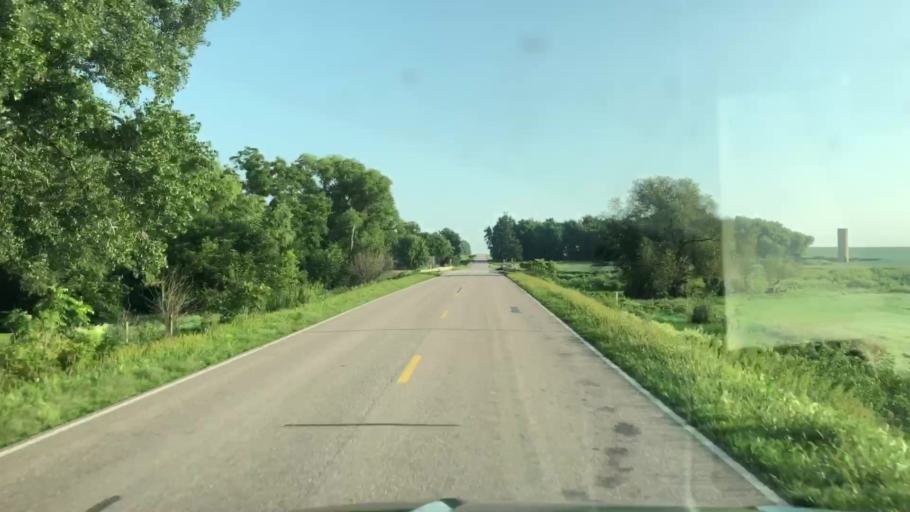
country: US
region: Iowa
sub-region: Lyon County
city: George
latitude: 43.2517
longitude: -96.0003
